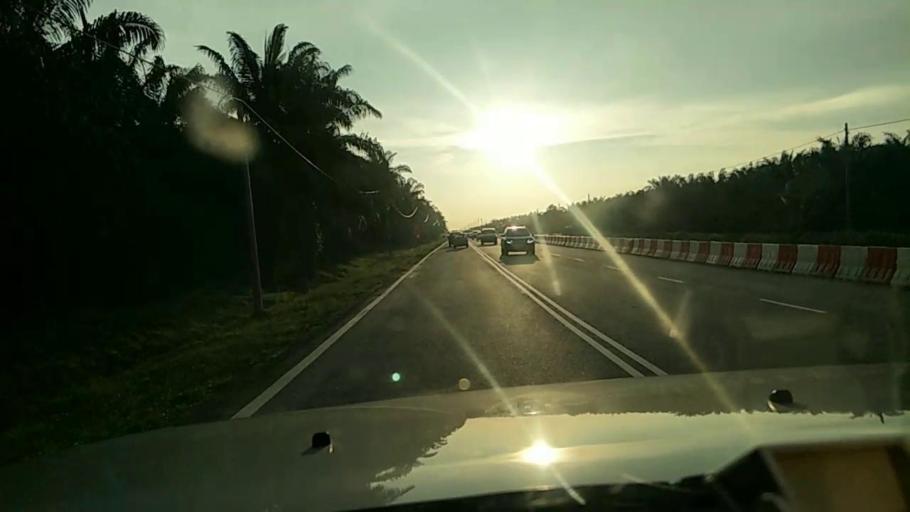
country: MY
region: Perak
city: Kampong Dungun
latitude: 3.3052
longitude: 101.3537
